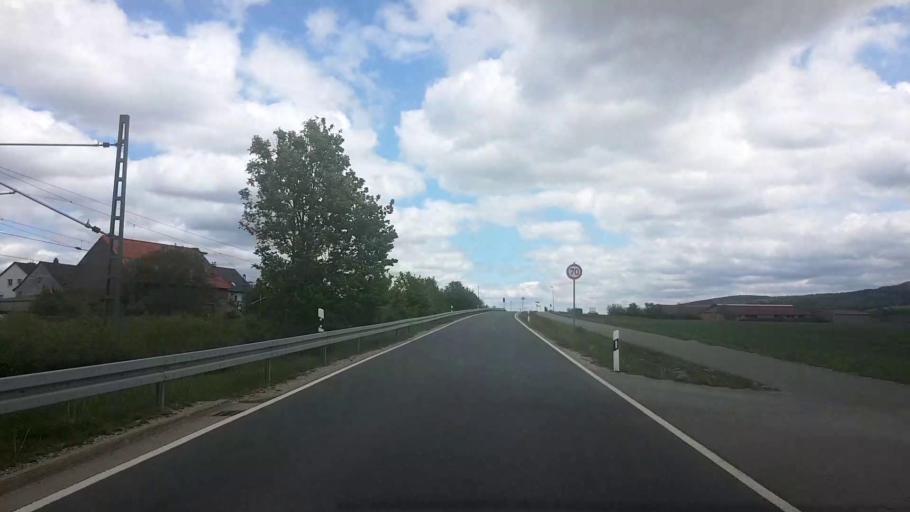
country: DE
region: Bavaria
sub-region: Upper Franconia
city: Bad Staffelstein
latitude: 50.1155
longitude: 11.0083
